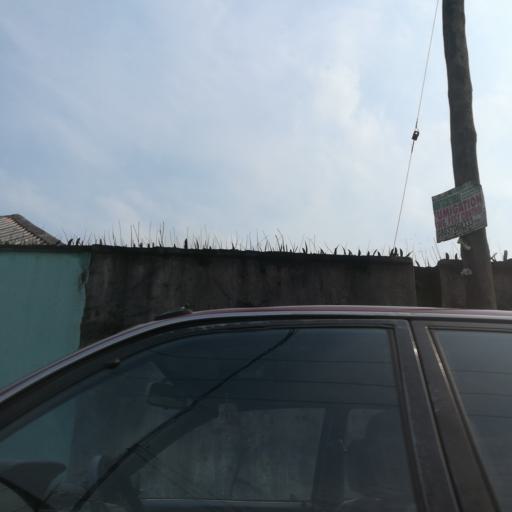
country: NG
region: Rivers
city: Port Harcourt
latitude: 4.8474
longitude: 7.0544
